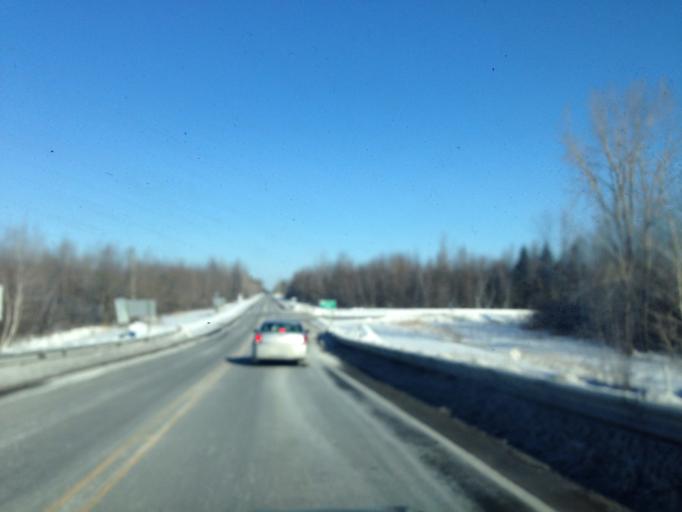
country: CA
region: Ontario
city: Clarence-Rockland
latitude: 45.3510
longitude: -75.4466
